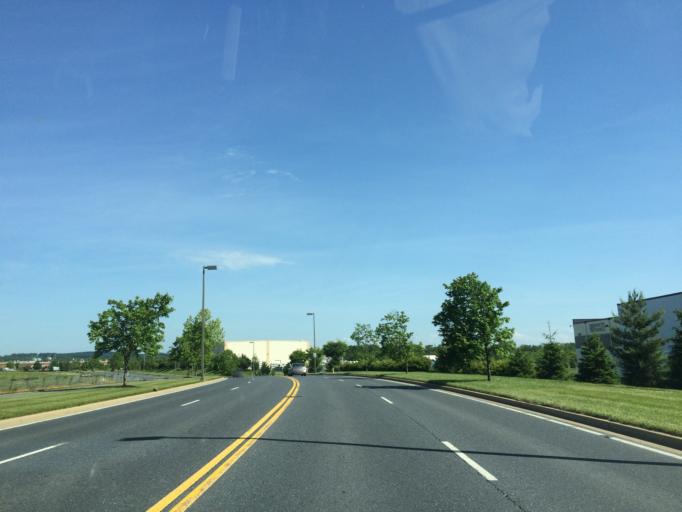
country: US
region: Maryland
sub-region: Frederick County
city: Frederick
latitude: 39.4402
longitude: -77.3816
